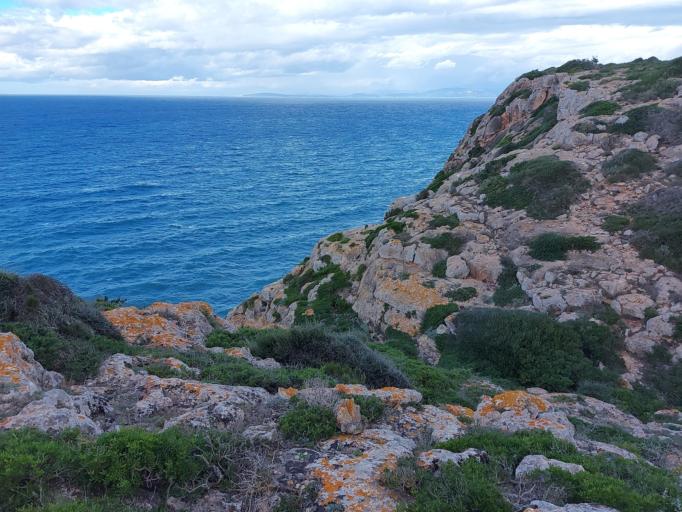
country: ES
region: Balearic Islands
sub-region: Illes Balears
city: s'Arenal
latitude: 39.3958
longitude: 2.7518
